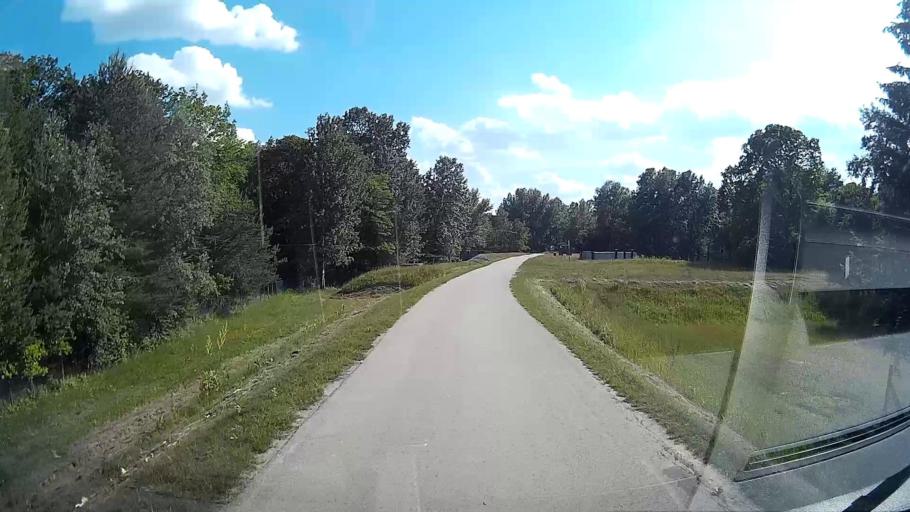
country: HU
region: Pest
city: God
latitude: 47.6632
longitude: 19.1097
